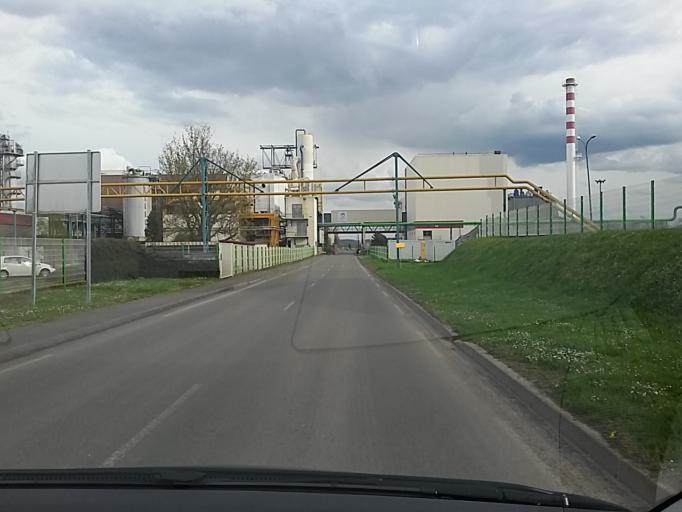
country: FR
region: Picardie
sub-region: Departement de l'Oise
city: Grandfresnoy
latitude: 49.3617
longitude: 2.6648
